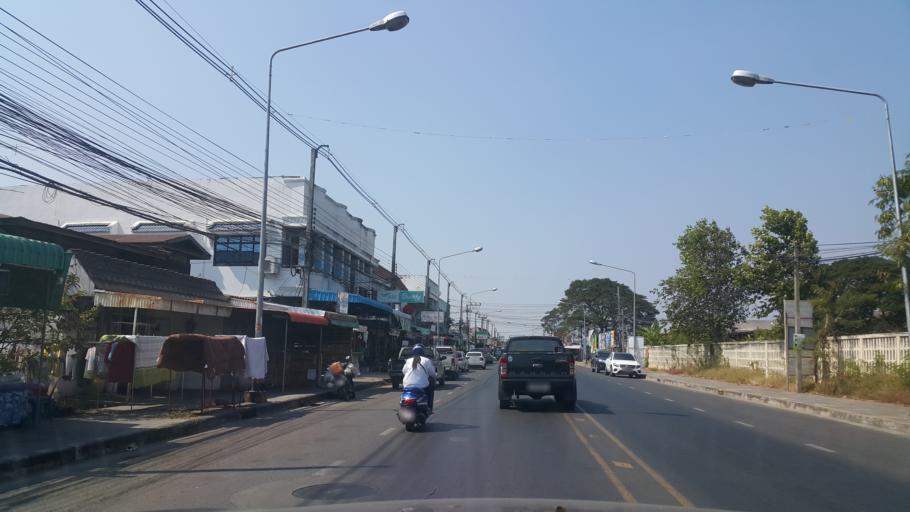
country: TH
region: Buriram
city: Satuek
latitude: 15.2945
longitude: 103.2892
